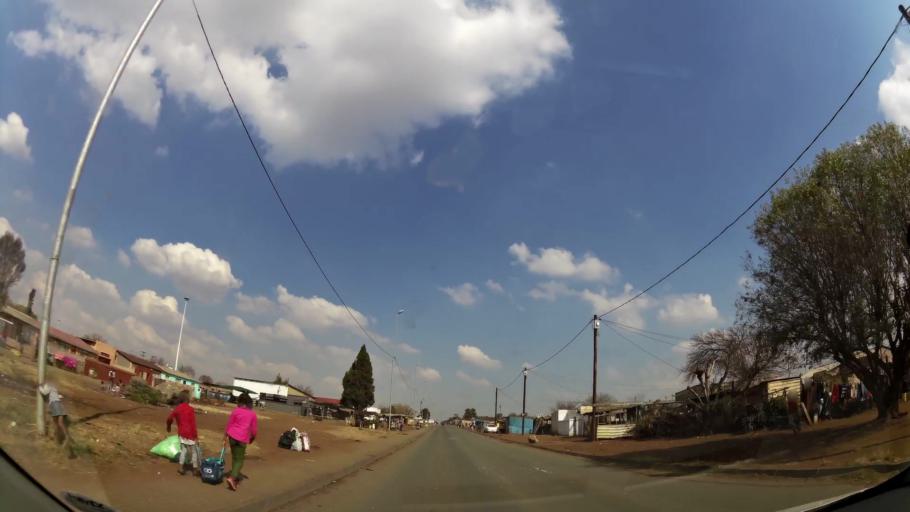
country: ZA
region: Gauteng
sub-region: Ekurhuleni Metropolitan Municipality
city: Germiston
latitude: -26.3069
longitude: 28.1487
